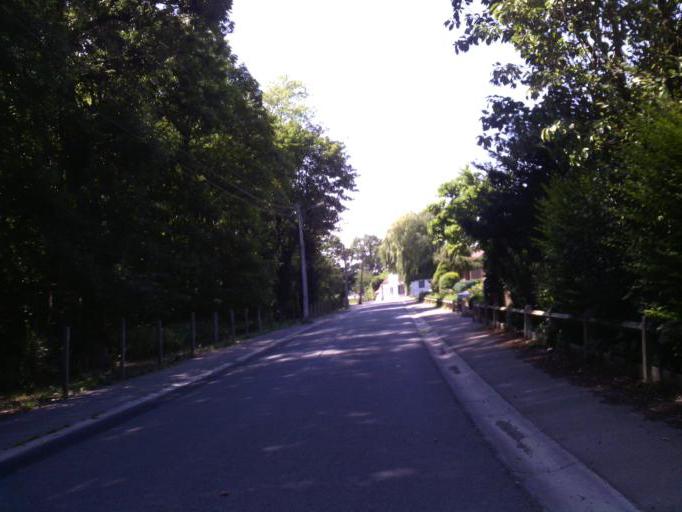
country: BE
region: Wallonia
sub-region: Province du Hainaut
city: Pecq
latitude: 50.6401
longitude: 3.3420
